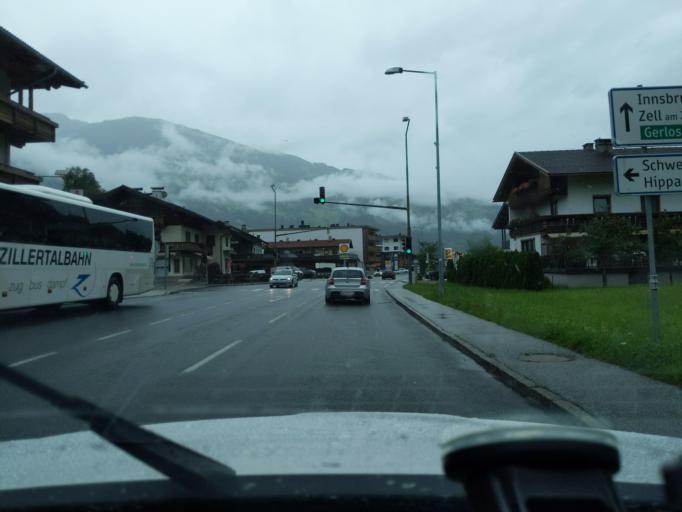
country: AT
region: Tyrol
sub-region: Politischer Bezirk Schwaz
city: Ramsau im Zillertal
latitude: 47.2040
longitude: 11.8708
